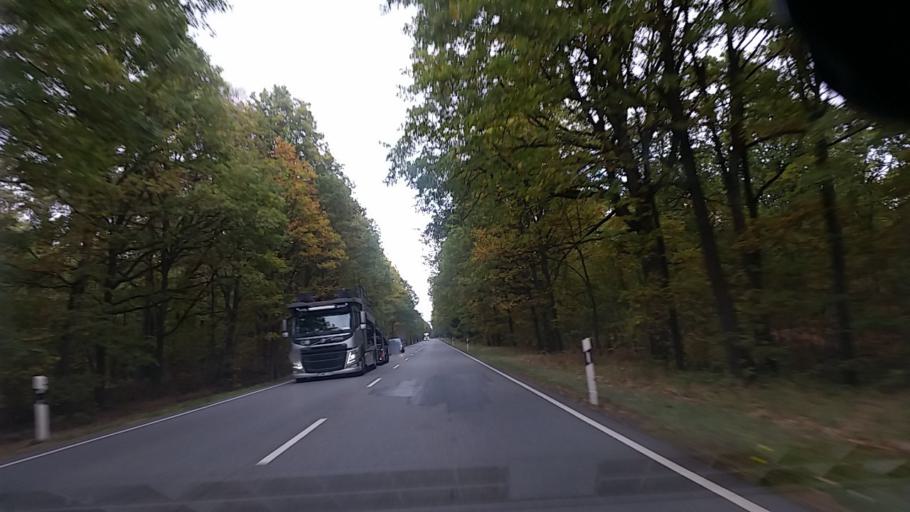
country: DE
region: Lower Saxony
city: Sprakensehl
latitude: 52.8136
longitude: 10.4874
